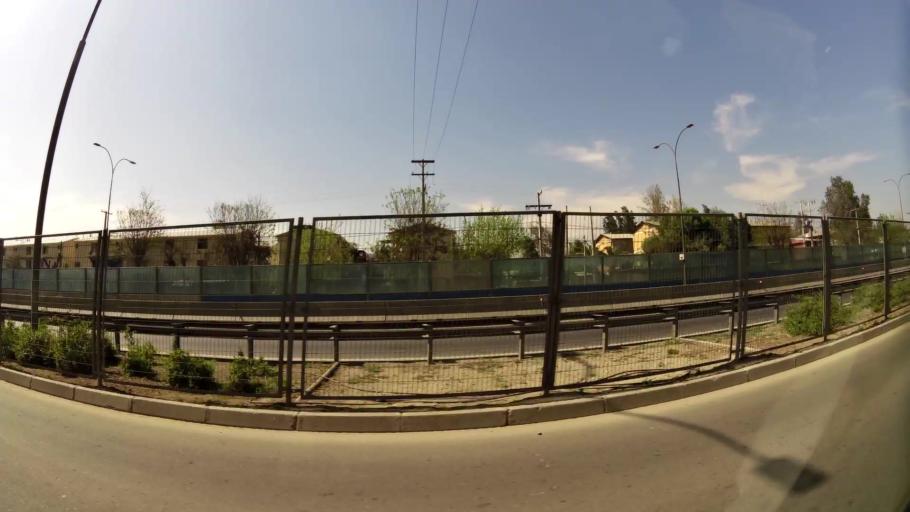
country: CL
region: Santiago Metropolitan
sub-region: Provincia de Santiago
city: Lo Prado
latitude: -33.3908
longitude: -70.6999
